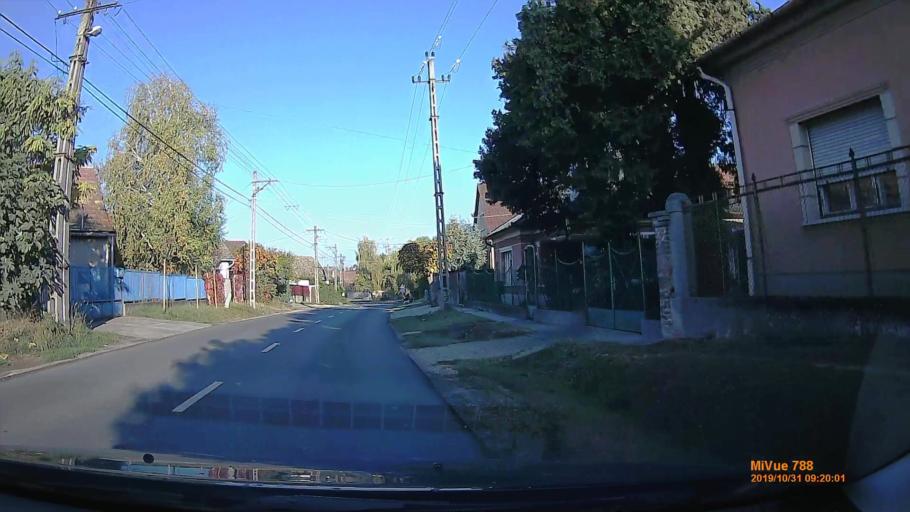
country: HU
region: Pest
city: Gyomro
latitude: 47.4210
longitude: 19.3879
